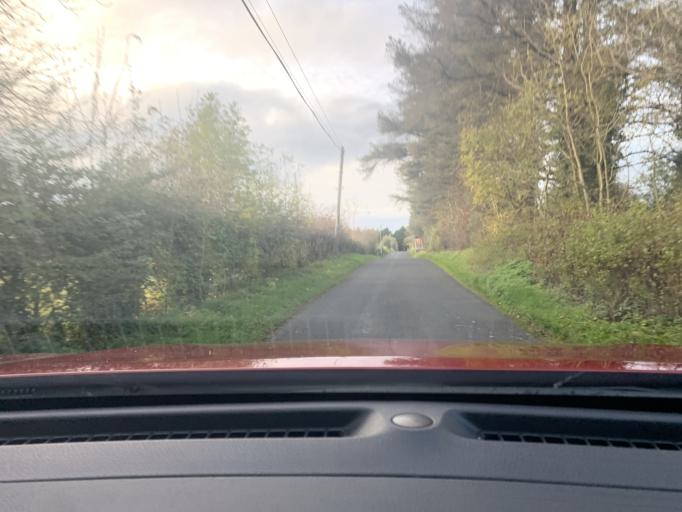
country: IE
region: Connaught
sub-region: Roscommon
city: Ballaghaderreen
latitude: 53.9120
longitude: -8.5852
